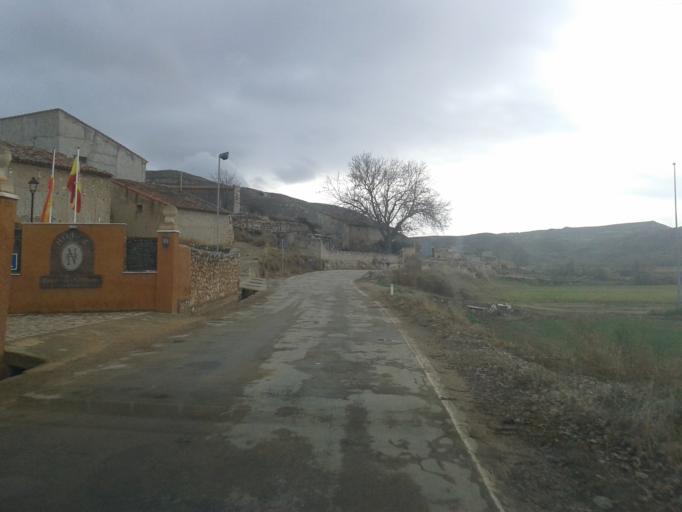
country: ES
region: Aragon
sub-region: Provincia de Teruel
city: Calamocha
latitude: 40.9287
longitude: -1.2564
